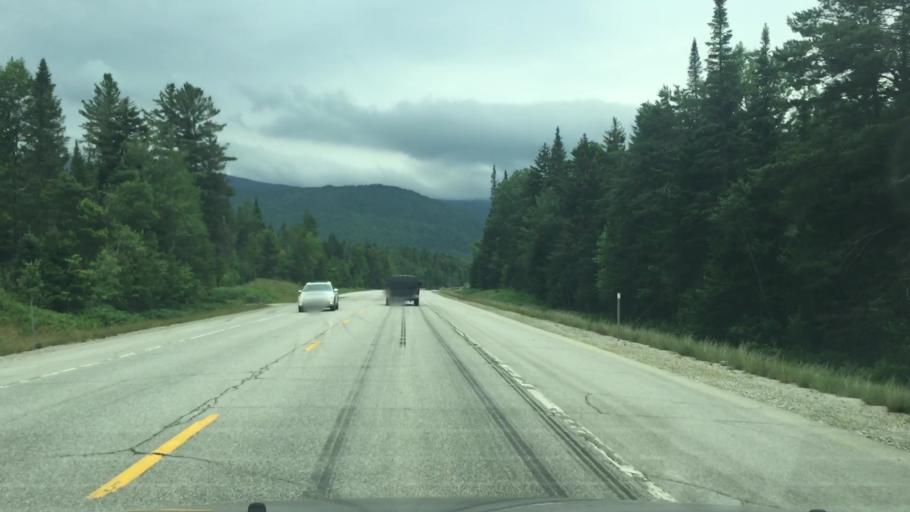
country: US
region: New Hampshire
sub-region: Coos County
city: Jefferson
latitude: 44.2448
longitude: -71.4328
